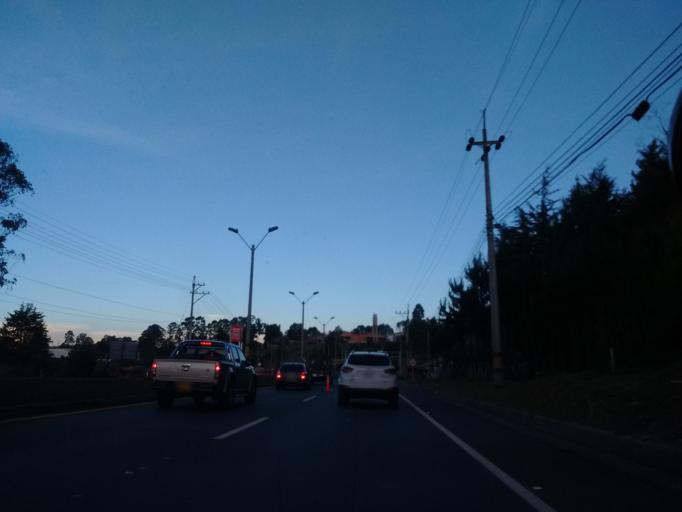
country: CO
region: Antioquia
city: Rionegro
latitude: 6.1808
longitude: -75.3698
